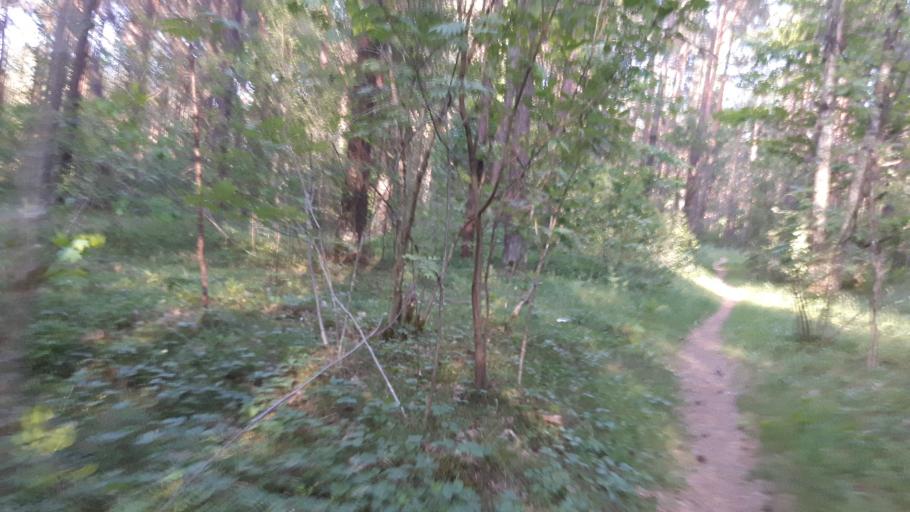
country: LV
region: Riga
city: Jaunciems
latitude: 57.0101
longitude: 24.1376
